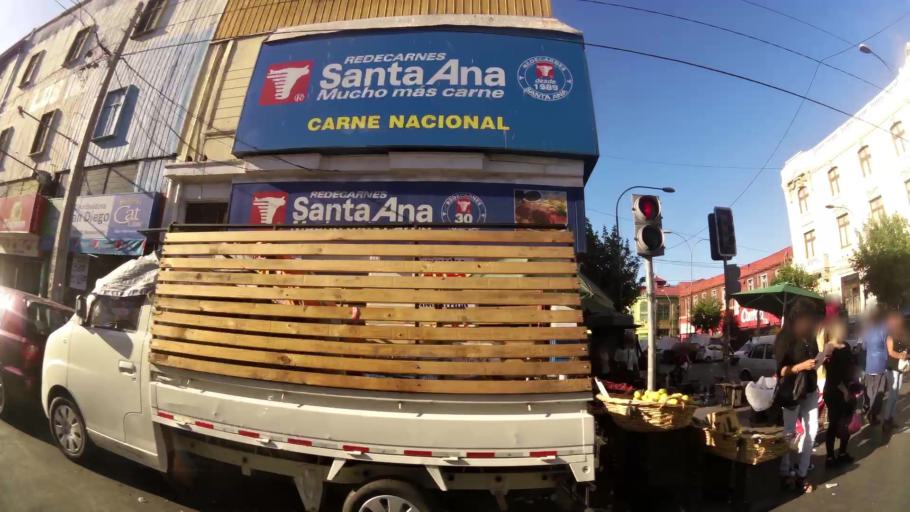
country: CL
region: Valparaiso
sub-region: Provincia de Valparaiso
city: Valparaiso
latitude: -33.0462
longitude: -71.6081
